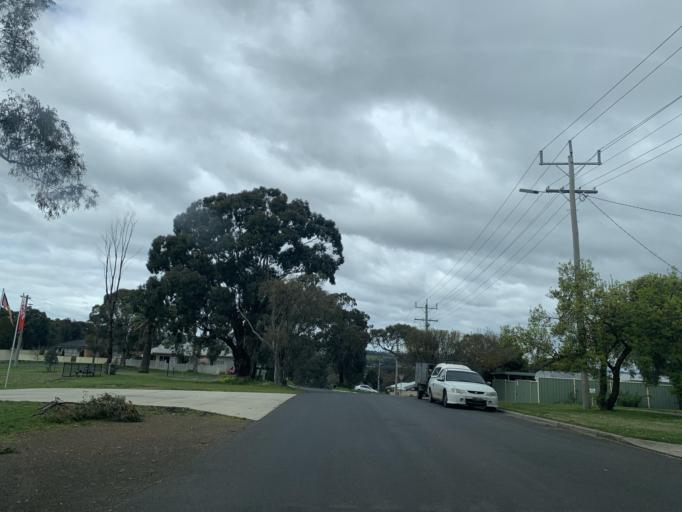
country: AU
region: Victoria
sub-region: Whittlesea
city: Whittlesea
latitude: -37.2079
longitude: 145.0475
